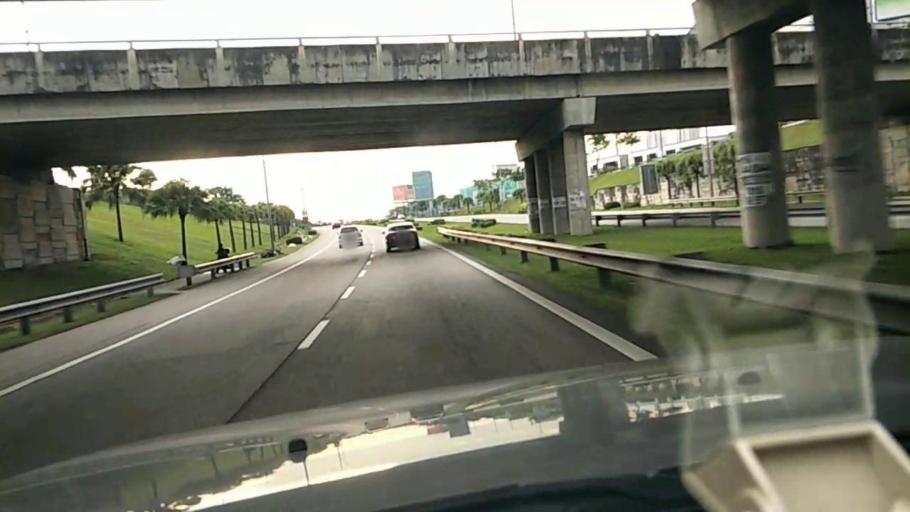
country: MY
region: Selangor
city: Shah Alam
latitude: 3.1043
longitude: 101.4699
